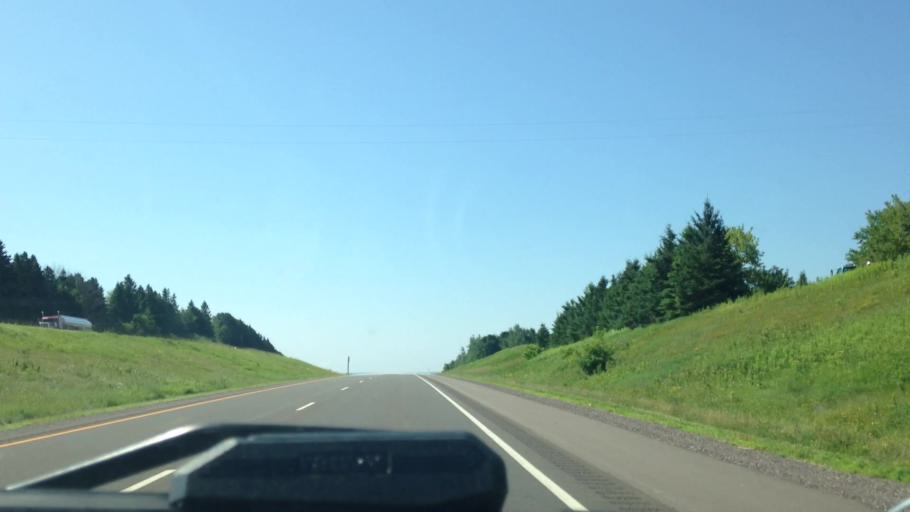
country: US
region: Wisconsin
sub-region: Washburn County
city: Spooner
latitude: 45.9608
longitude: -91.8283
